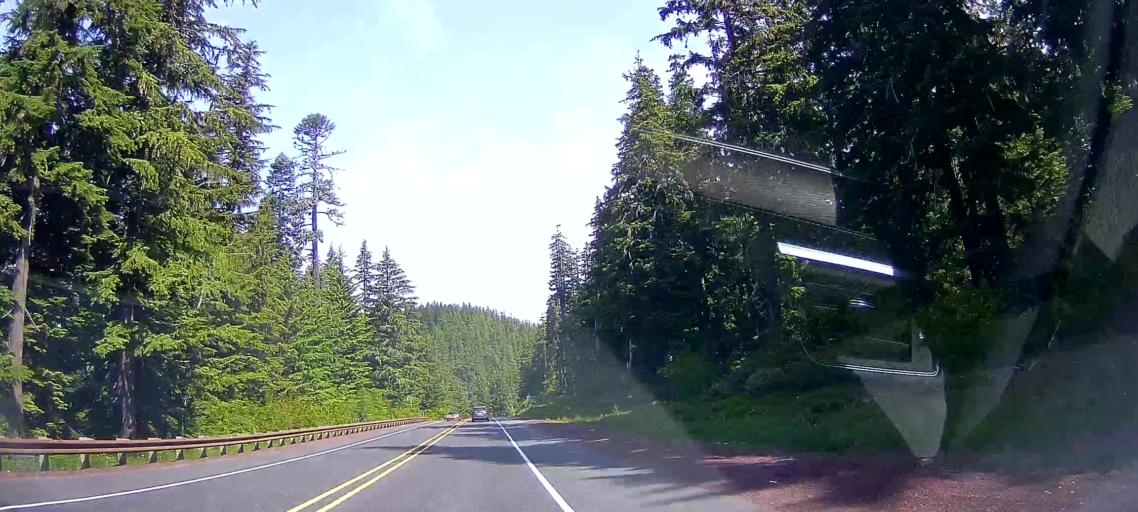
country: US
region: Oregon
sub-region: Clackamas County
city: Mount Hood Village
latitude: 45.2063
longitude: -121.6969
